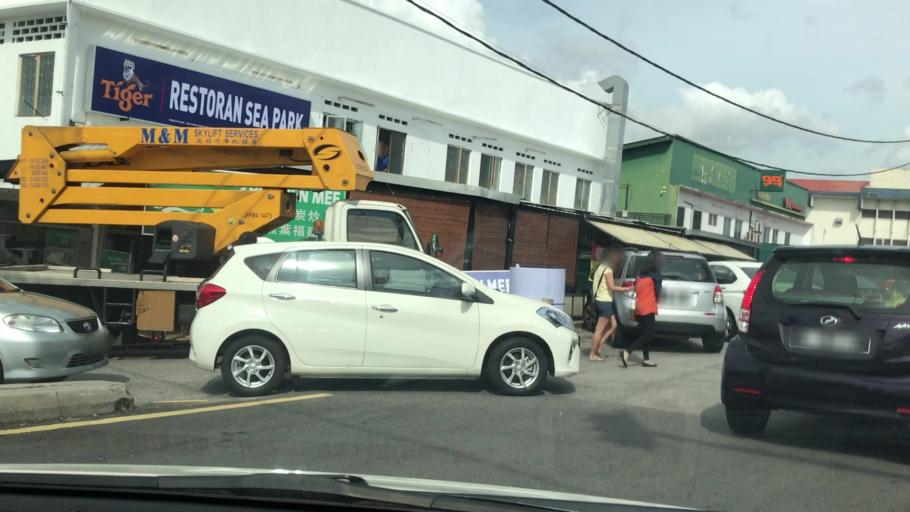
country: MY
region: Selangor
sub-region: Petaling
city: Petaling Jaya
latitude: 3.1089
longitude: 101.6229
